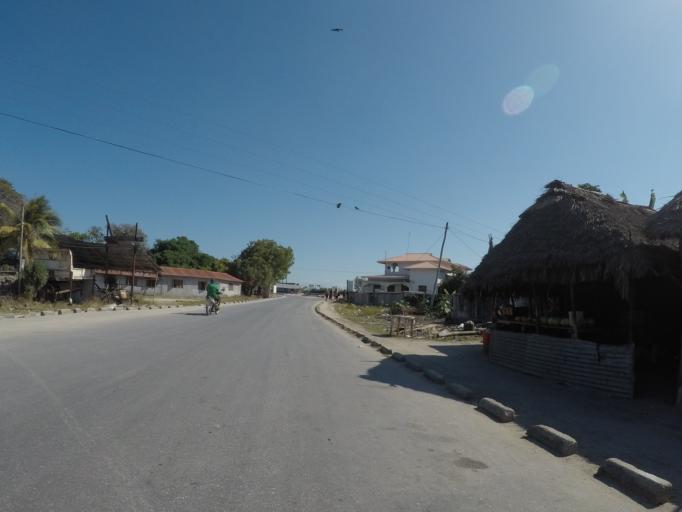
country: TZ
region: Zanzibar Central/South
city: Nganane
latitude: -6.2658
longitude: 39.5318
